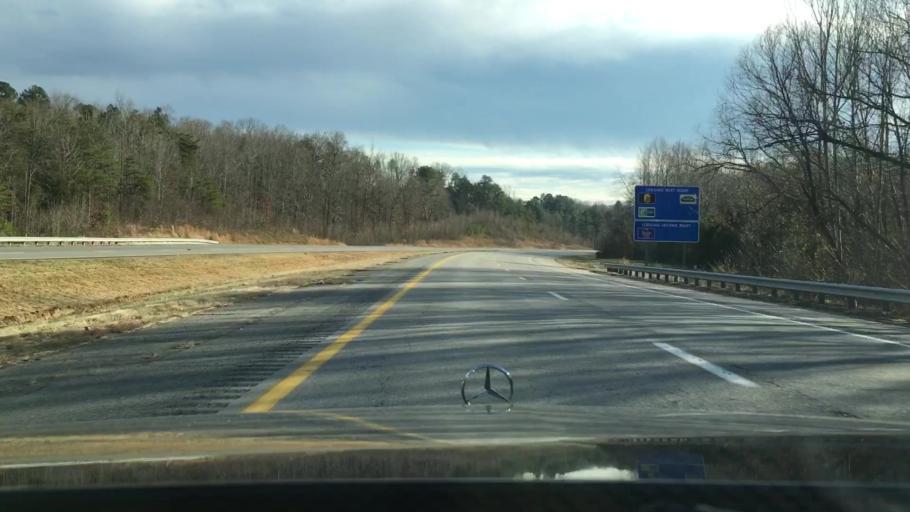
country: US
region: Virginia
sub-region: City of Danville
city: Danville
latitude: 36.6047
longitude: -79.3572
